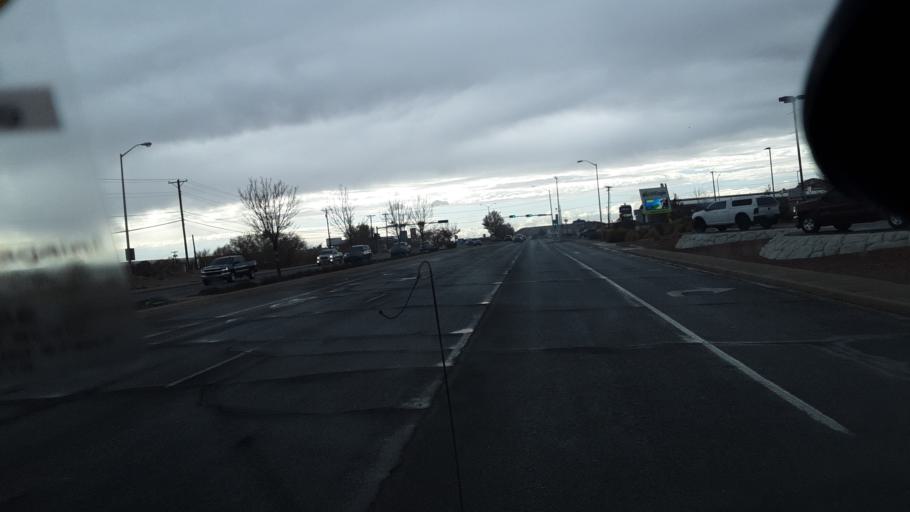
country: US
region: New Mexico
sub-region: San Juan County
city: Flora Vista
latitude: 36.7724
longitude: -108.1375
